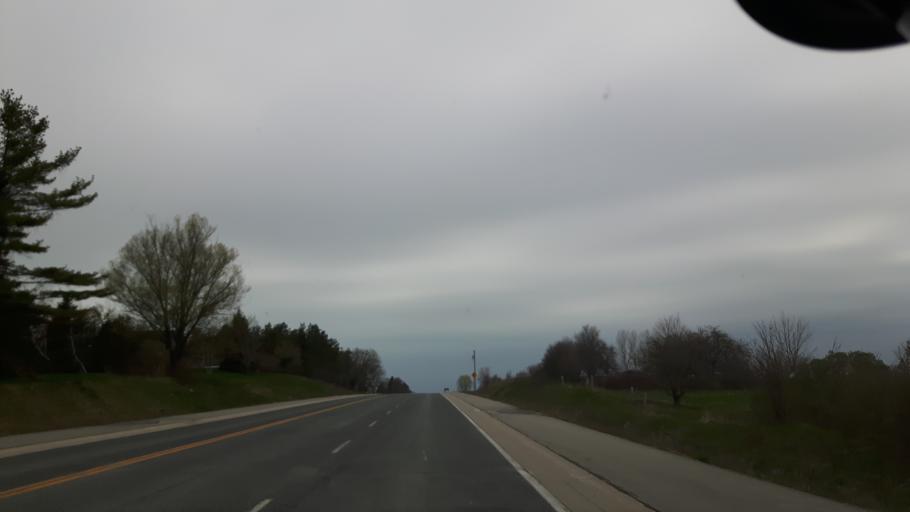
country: CA
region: Ontario
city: Goderich
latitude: 43.6493
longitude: -81.6059
